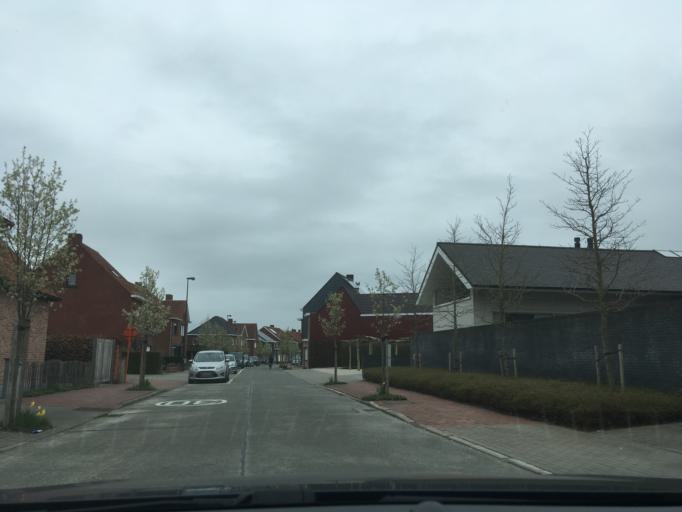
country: BE
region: Flanders
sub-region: Provincie West-Vlaanderen
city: Lichtervelde
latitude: 51.0256
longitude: 3.1295
